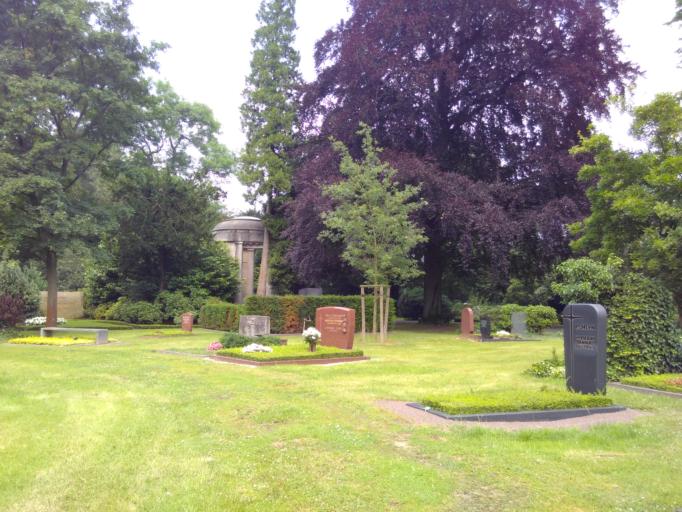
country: DE
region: North Rhine-Westphalia
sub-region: Regierungsbezirk Dusseldorf
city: Dusseldorf
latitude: 51.2578
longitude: 6.7718
